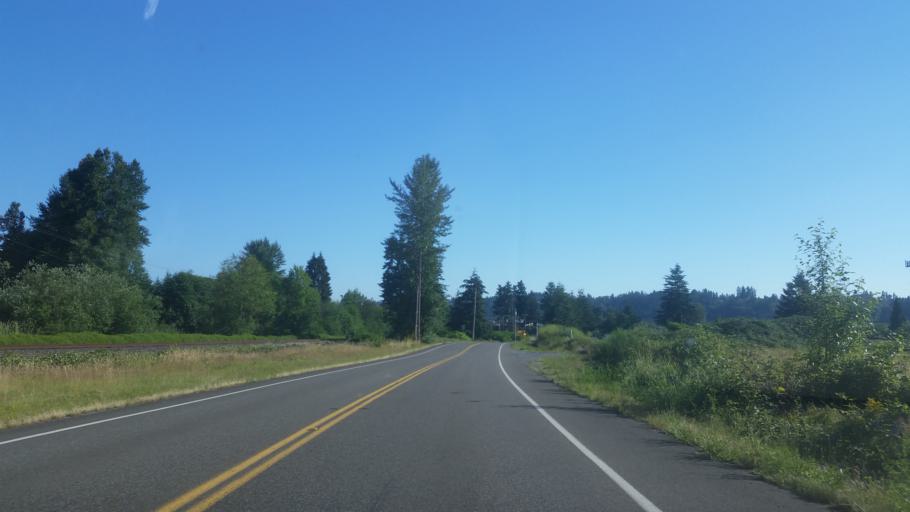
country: US
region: Washington
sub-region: King County
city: Woodinville
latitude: 47.7619
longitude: -122.1548
